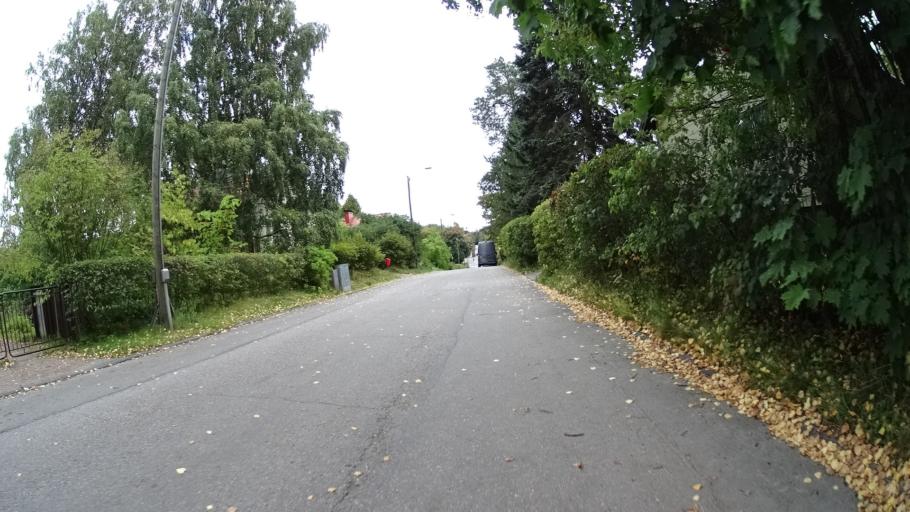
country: FI
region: Uusimaa
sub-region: Helsinki
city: Helsinki
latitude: 60.2325
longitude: 24.9186
